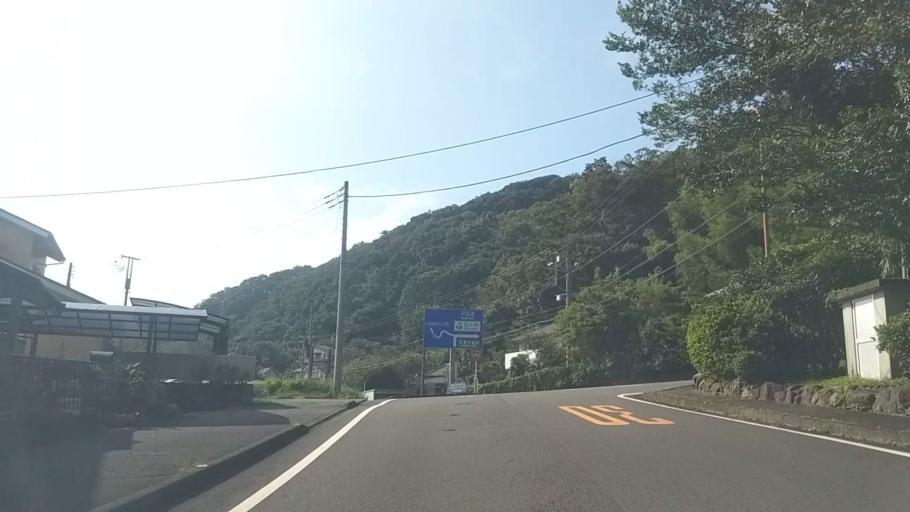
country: JP
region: Shizuoka
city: Heda
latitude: 34.9705
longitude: 138.9184
